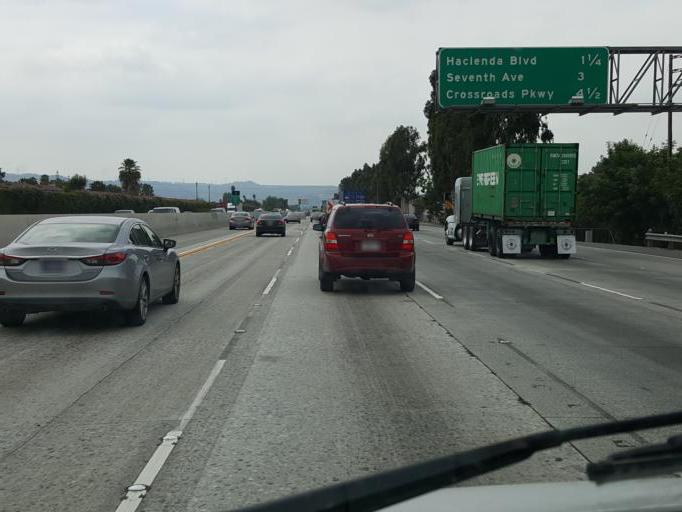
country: US
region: California
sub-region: Los Angeles County
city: La Puente
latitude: 33.9991
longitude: -117.9387
